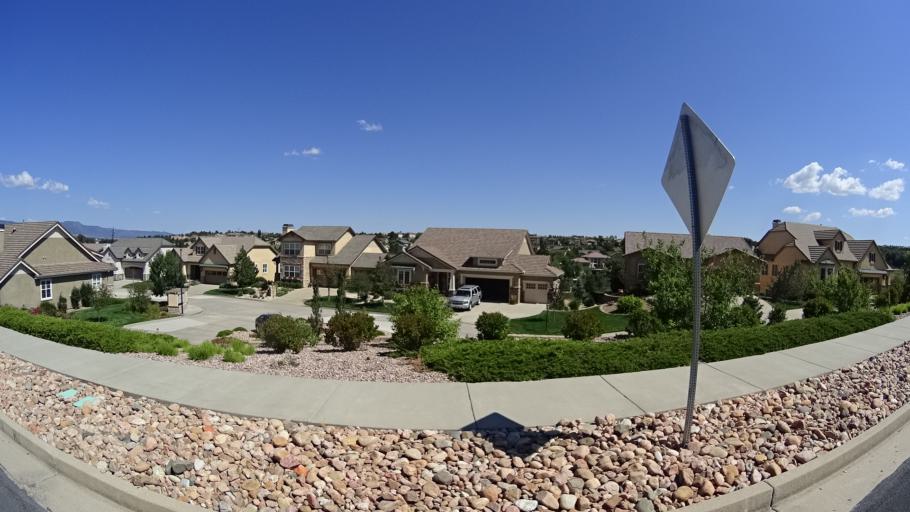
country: US
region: Colorado
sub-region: El Paso County
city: Air Force Academy
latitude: 38.9691
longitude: -104.7801
